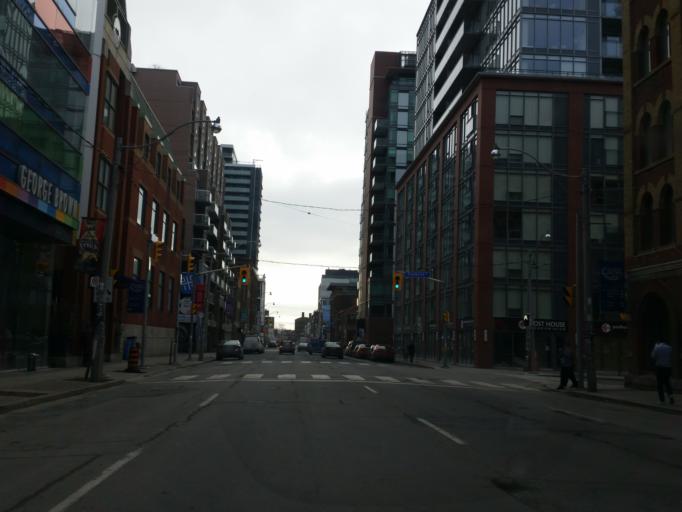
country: CA
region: Ontario
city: Toronto
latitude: 43.6518
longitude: -79.3703
